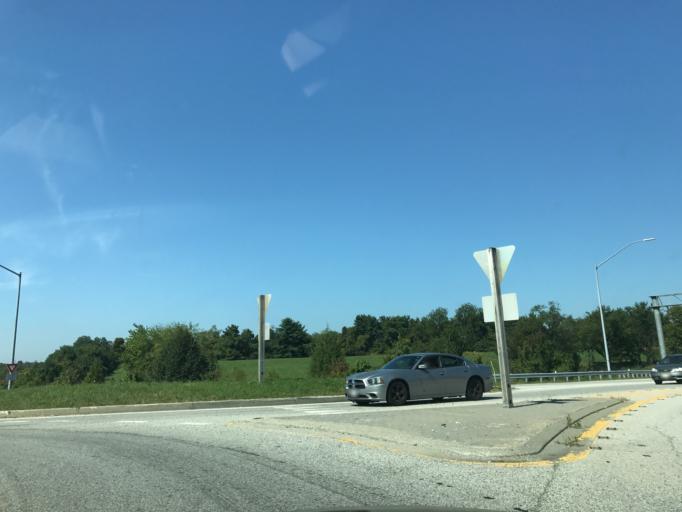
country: US
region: Maryland
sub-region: Howard County
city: Ilchester
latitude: 39.2086
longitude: -76.7829
